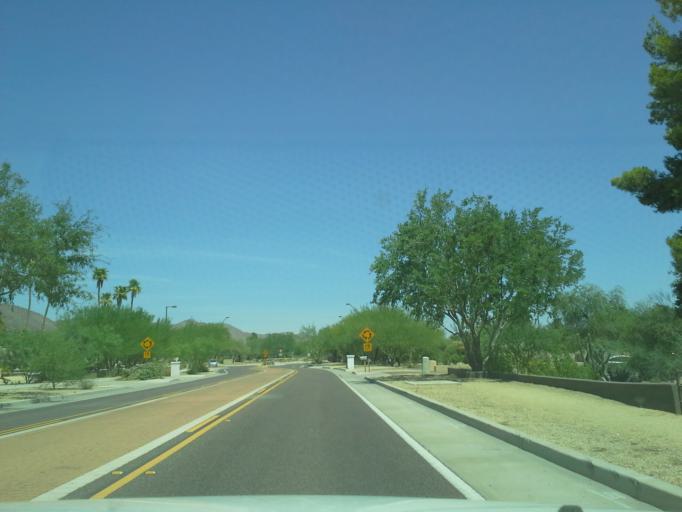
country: US
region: Arizona
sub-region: Maricopa County
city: Scottsdale
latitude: 33.5970
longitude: -111.8671
